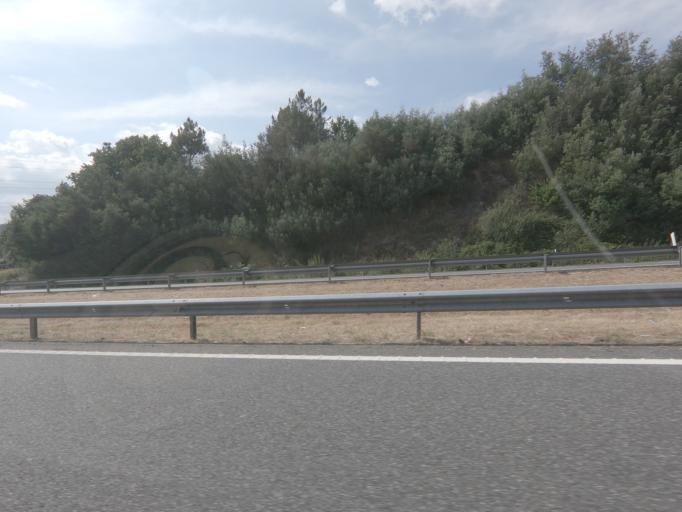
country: ES
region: Galicia
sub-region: Provincia de Ourense
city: Castrelo de Mino
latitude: 42.3172
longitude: -8.0790
